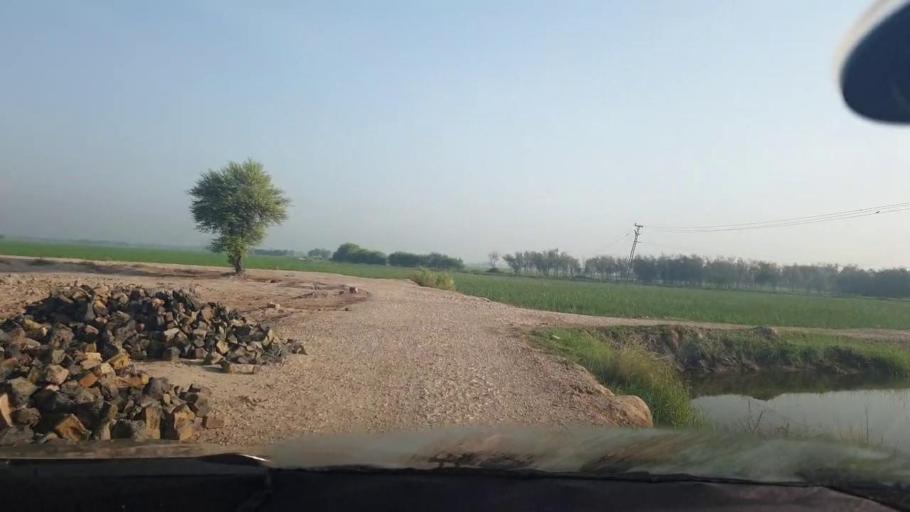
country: PK
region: Sindh
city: Kambar
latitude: 27.6334
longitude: 68.0166
